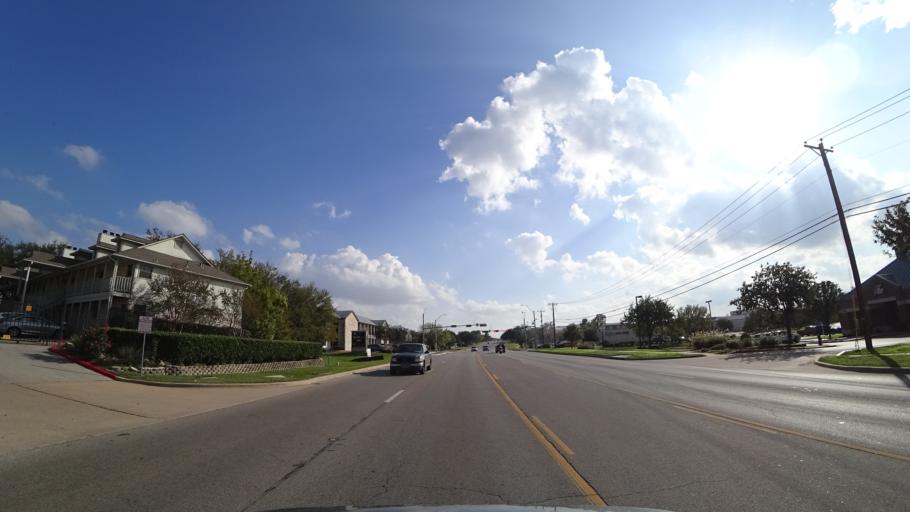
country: US
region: Texas
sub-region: Williamson County
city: Round Rock
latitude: 30.5010
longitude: -97.6762
